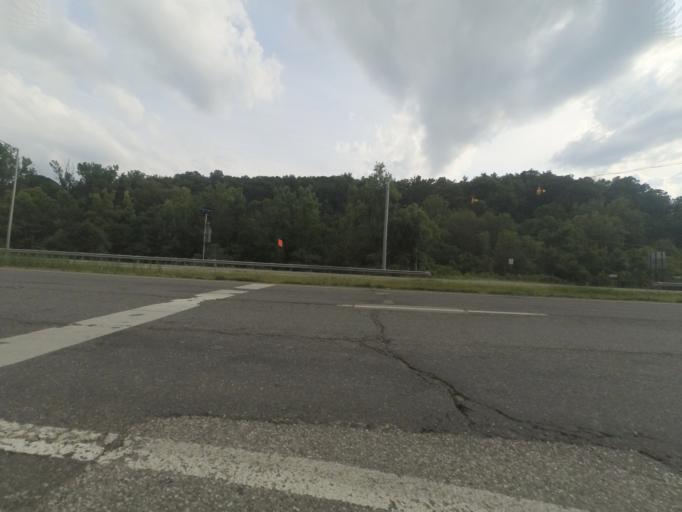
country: US
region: West Virginia
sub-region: Cabell County
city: Huntington
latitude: 38.3921
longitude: -82.4014
